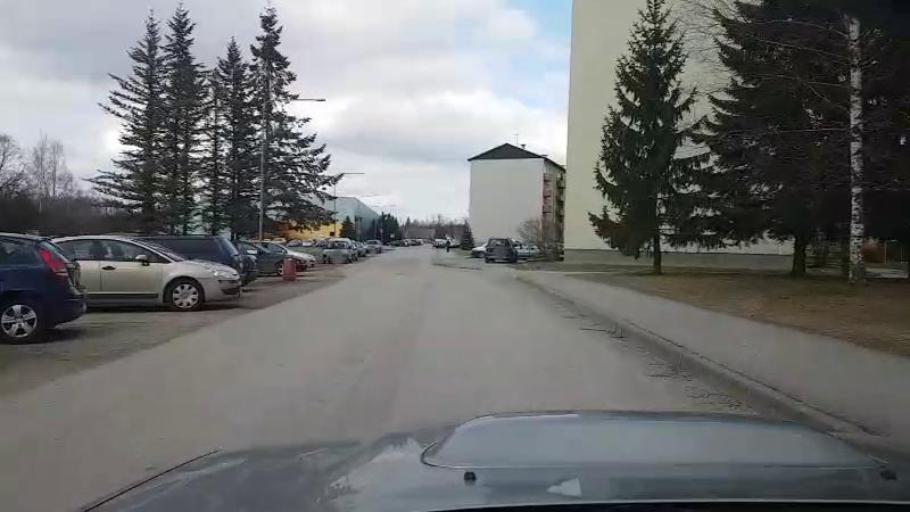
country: EE
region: Jaervamaa
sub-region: Paide linn
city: Paide
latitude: 58.8850
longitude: 25.5382
